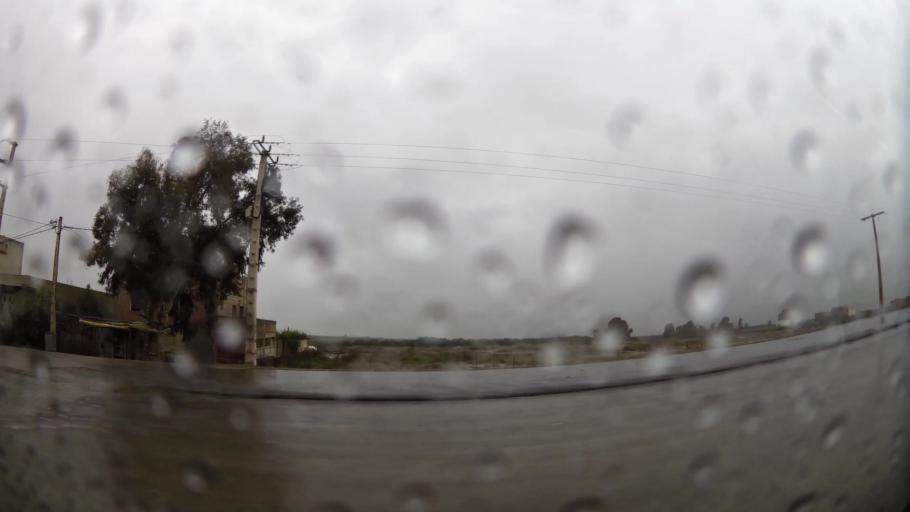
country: MA
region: Oriental
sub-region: Nador
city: Midar
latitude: 34.8795
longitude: -3.7262
